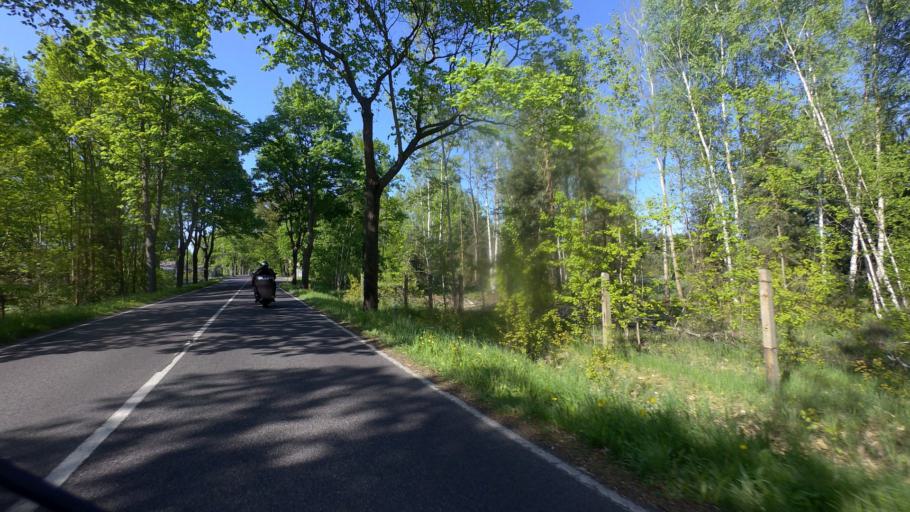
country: DE
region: Brandenburg
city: Bestensee
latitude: 52.2314
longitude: 13.6687
